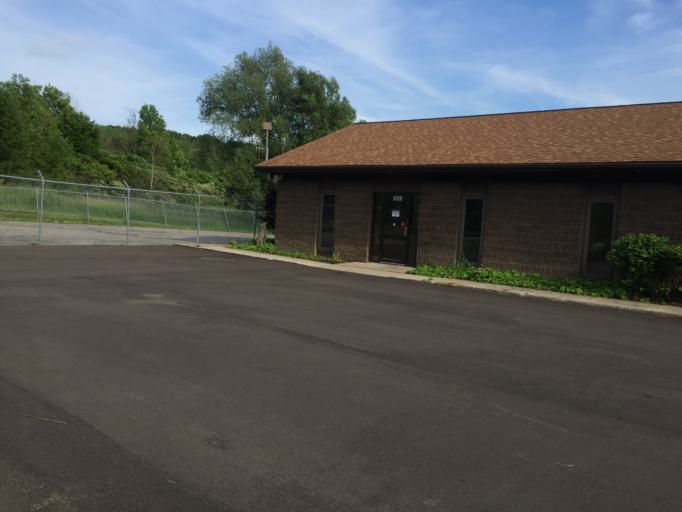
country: US
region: New York
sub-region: Erie County
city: East Aurora
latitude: 42.7536
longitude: -78.6057
